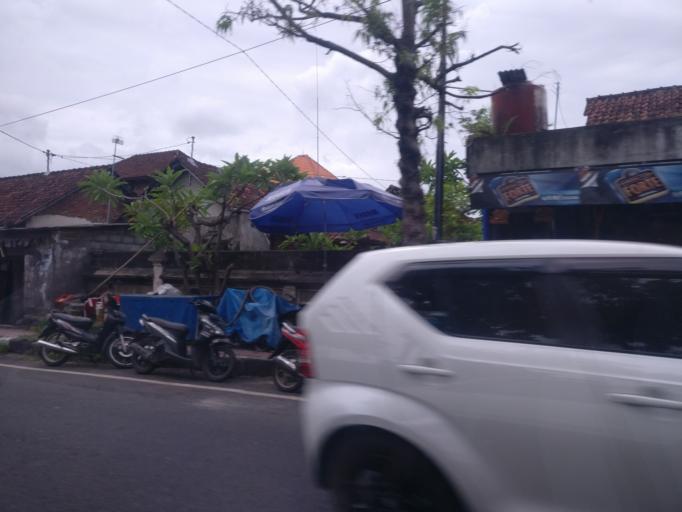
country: ID
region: Bali
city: Banjar Sedang
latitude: -8.5635
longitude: 115.3008
